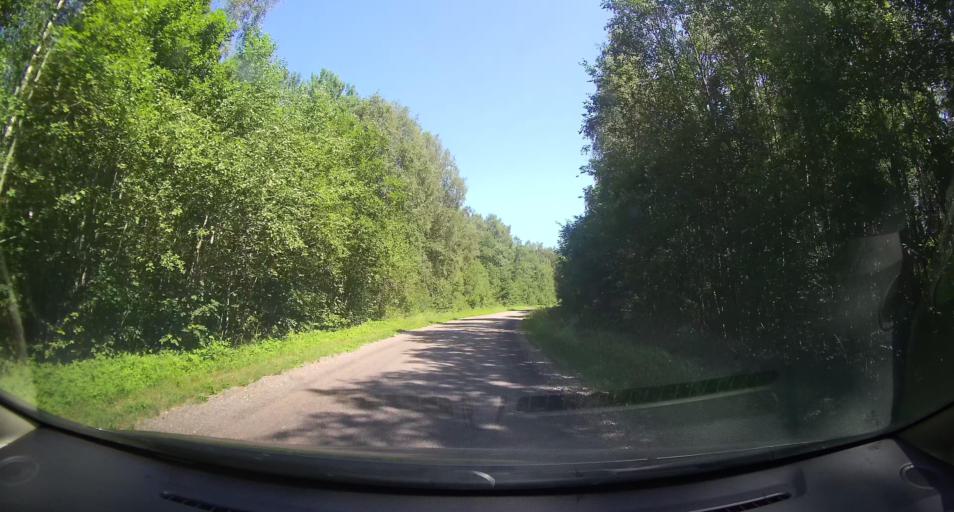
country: EE
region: Laeaene
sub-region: Lihula vald
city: Lihula
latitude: 58.6263
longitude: 23.6475
